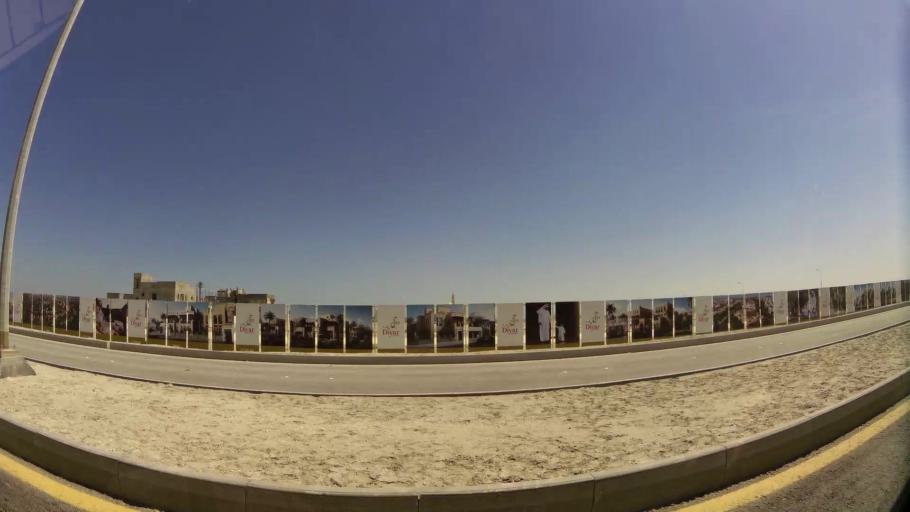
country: BH
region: Muharraq
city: Al Muharraq
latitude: 26.2987
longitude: 50.6372
